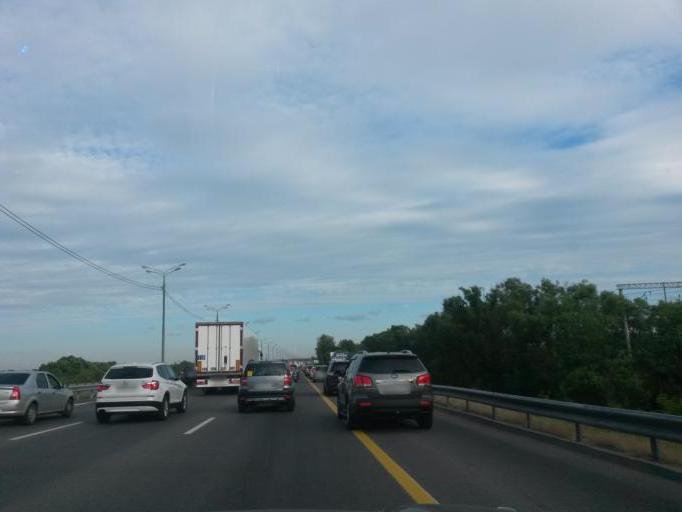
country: RU
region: Moskovskaya
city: Yam
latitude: 55.5110
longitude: 37.7160
